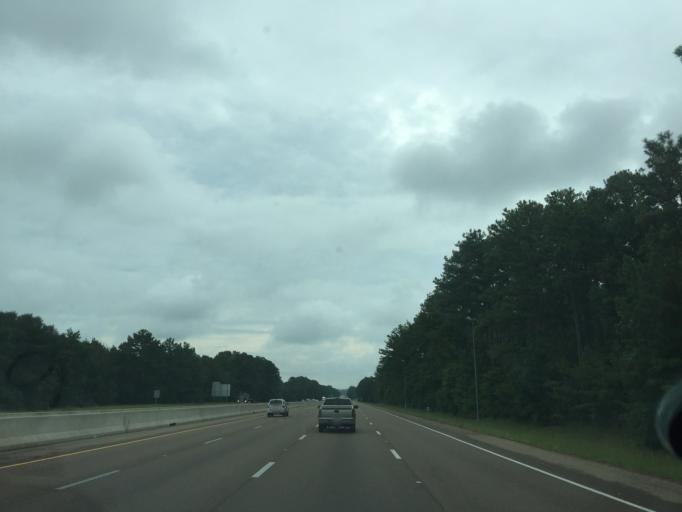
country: US
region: Mississippi
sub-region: Rankin County
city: Pearl
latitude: 32.2719
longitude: -90.0698
